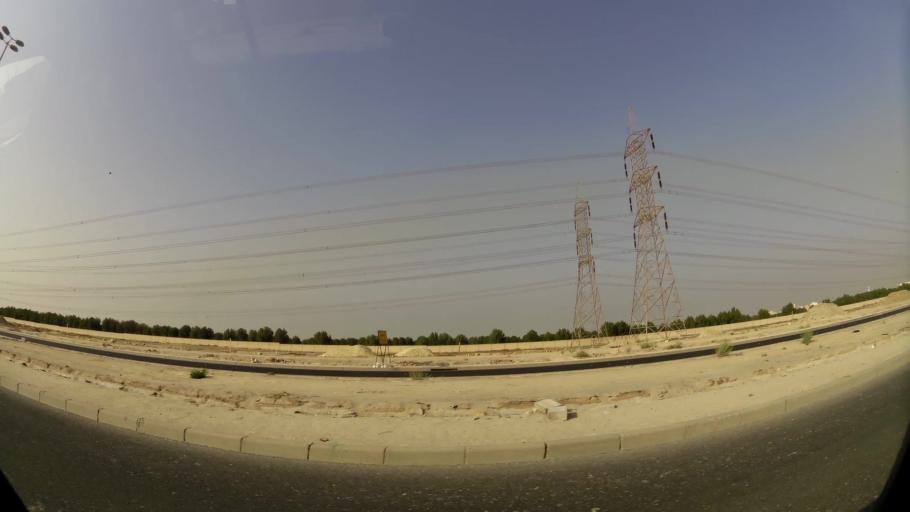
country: KW
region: Al Asimah
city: Ar Rabiyah
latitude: 29.2950
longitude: 47.8471
